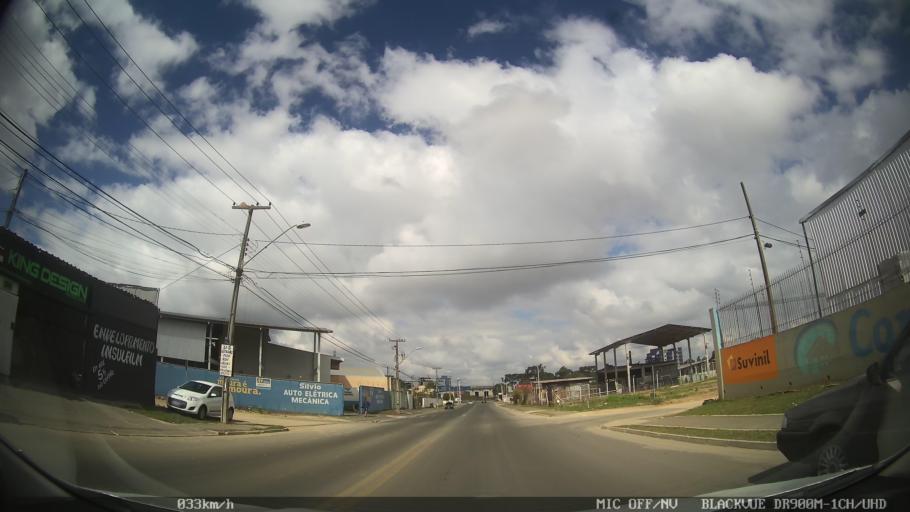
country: BR
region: Parana
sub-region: Pinhais
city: Pinhais
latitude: -25.3715
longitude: -49.1941
